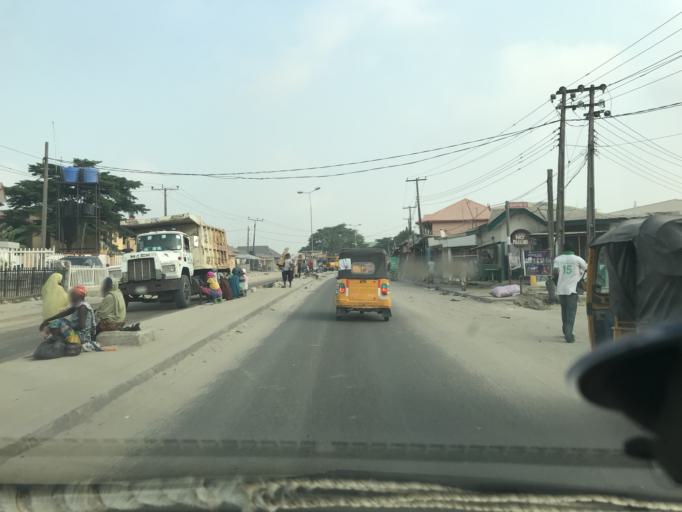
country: NG
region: Lagos
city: Ikoyi
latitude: 6.4708
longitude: 3.5654
